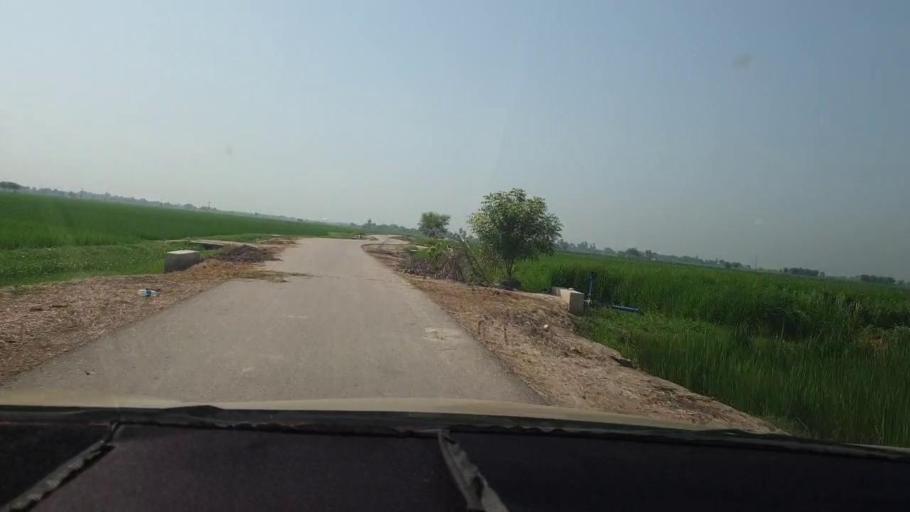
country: PK
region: Sindh
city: Kambar
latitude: 27.5670
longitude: 68.0445
